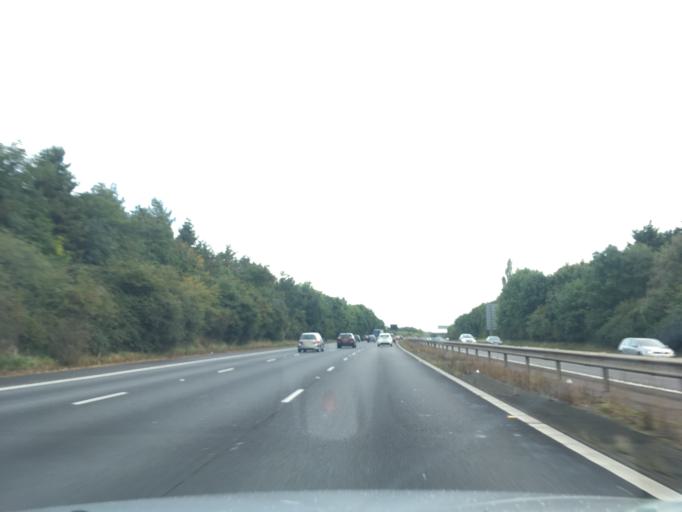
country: GB
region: England
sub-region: Oxfordshire
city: Bicester
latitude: 51.8877
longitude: -1.2053
